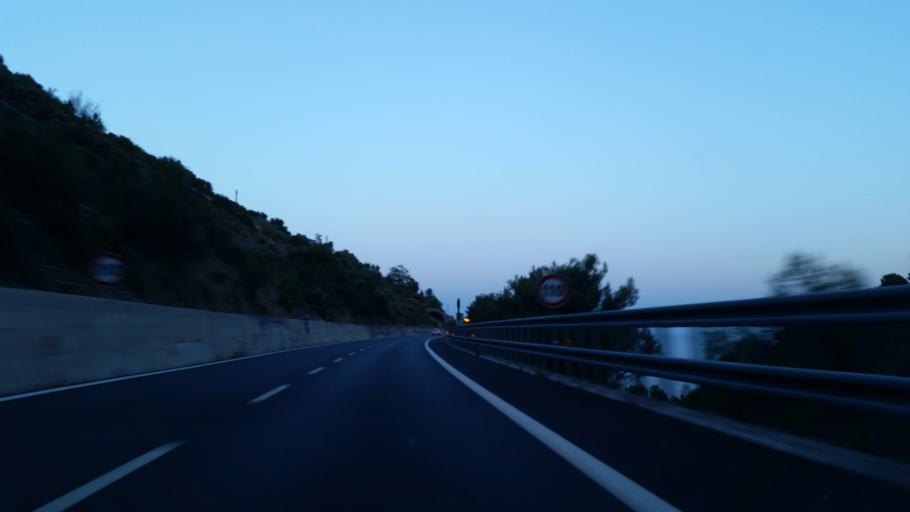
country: FR
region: Provence-Alpes-Cote d'Azur
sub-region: Departement des Alpes-Maritimes
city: Menton
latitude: 43.7892
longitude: 7.5451
